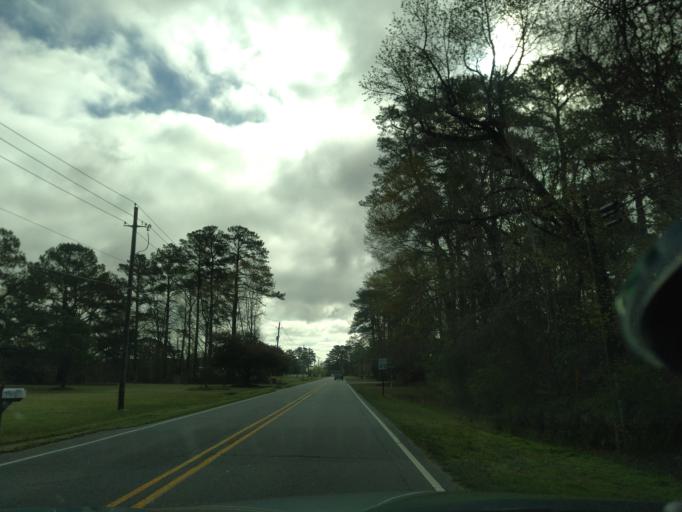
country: US
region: North Carolina
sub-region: Chowan County
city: Edenton
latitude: 36.0573
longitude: -76.6596
